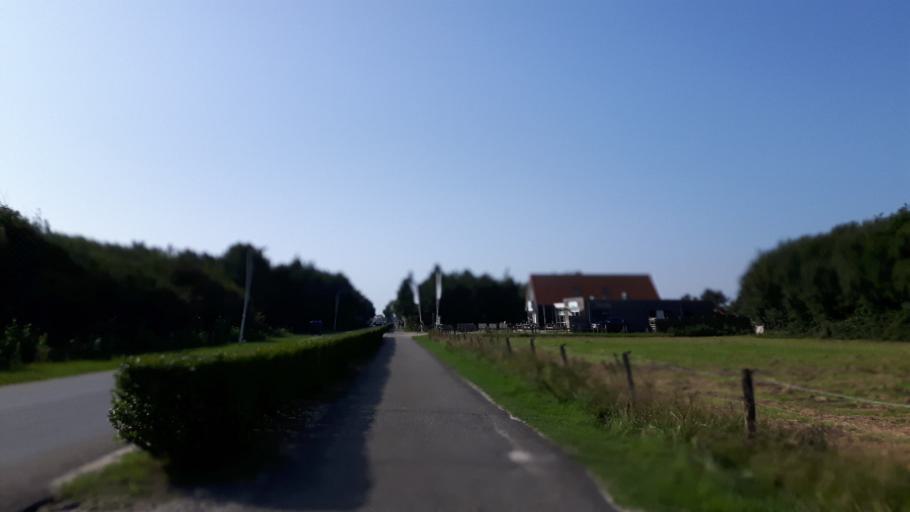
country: NL
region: Friesland
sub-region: Gemeente Ameland
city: Nes
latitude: 53.4562
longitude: 5.8043
